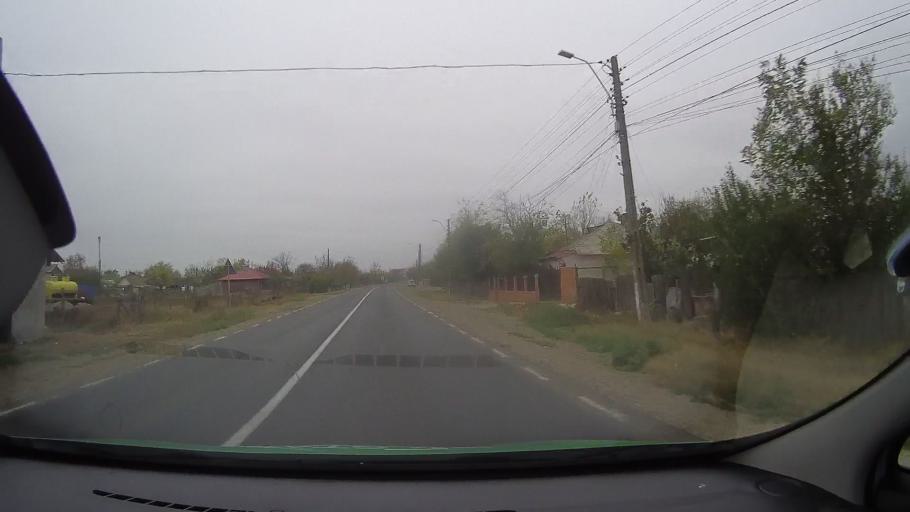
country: RO
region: Braila
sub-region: Comuna Baraganul
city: Baraganul
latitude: 44.8018
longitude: 27.5131
